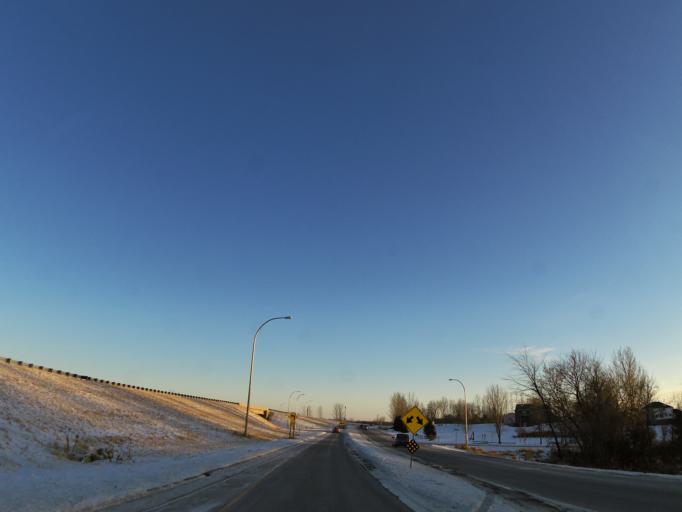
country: US
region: Minnesota
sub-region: Scott County
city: Shakopee
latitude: 44.7476
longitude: -93.5024
